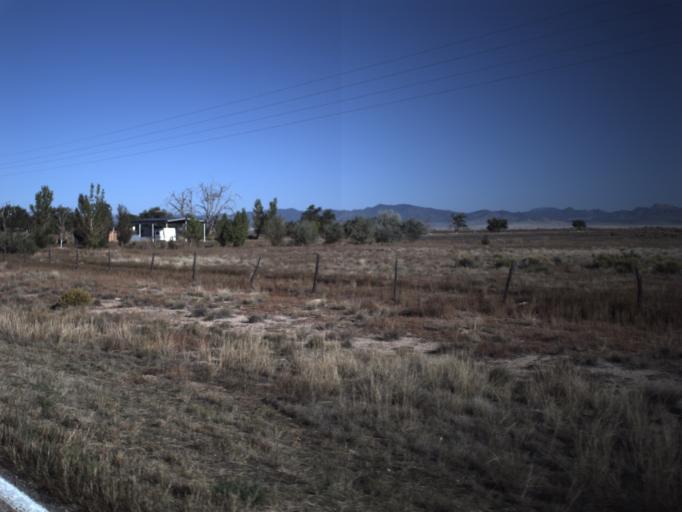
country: US
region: Utah
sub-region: Washington County
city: Enterprise
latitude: 37.7236
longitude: -113.6956
